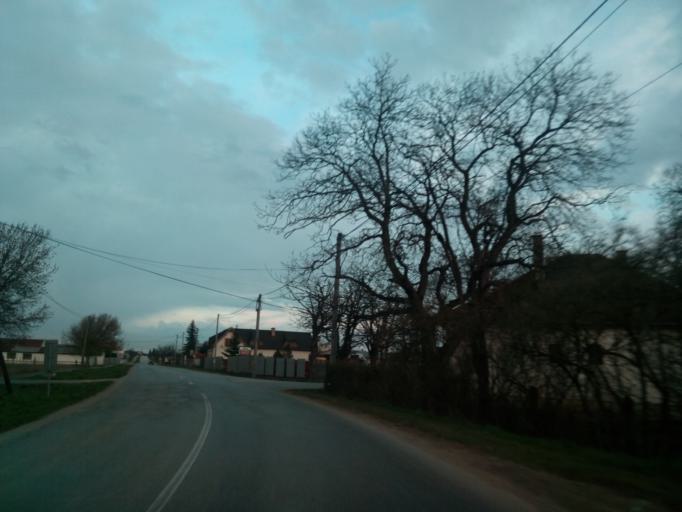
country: SK
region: Kosicky
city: Moldava nad Bodvou
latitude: 48.6034
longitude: 21.0016
